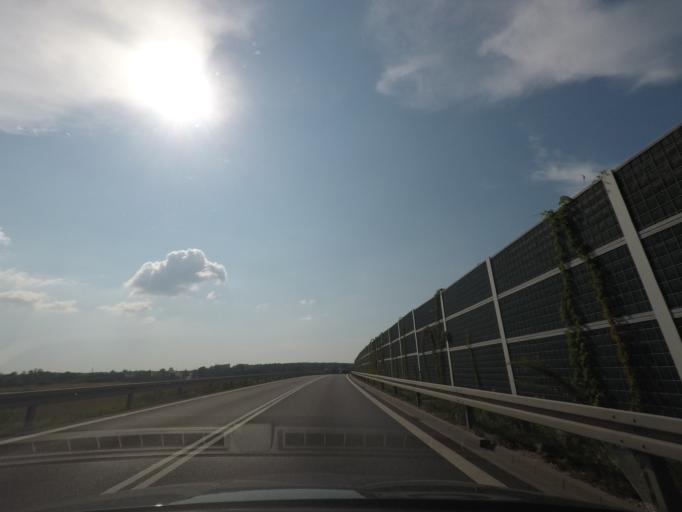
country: PL
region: Silesian Voivodeship
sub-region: Powiat pszczynski
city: Czarkow
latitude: 50.0015
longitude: 18.9185
